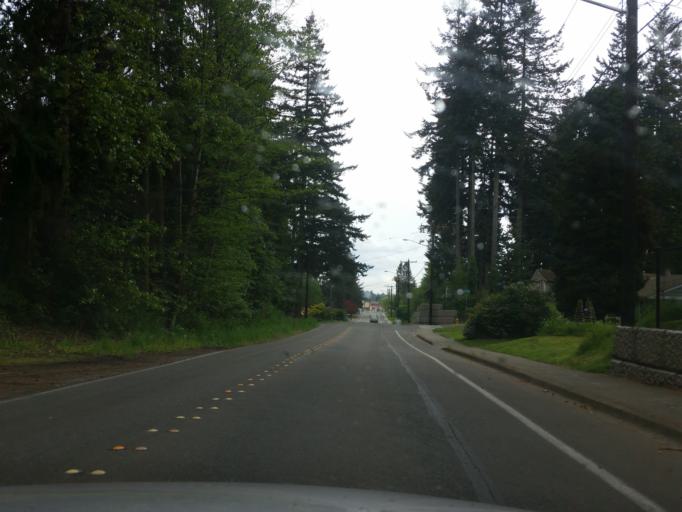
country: US
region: Washington
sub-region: Snohomish County
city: Lynnwood
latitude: 47.8274
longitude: -122.3143
